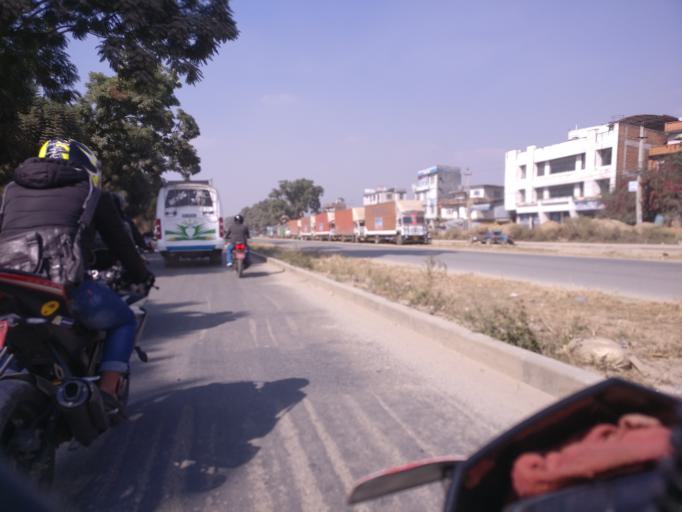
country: NP
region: Central Region
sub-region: Bagmati Zone
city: Patan
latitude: 27.6594
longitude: 85.3206
